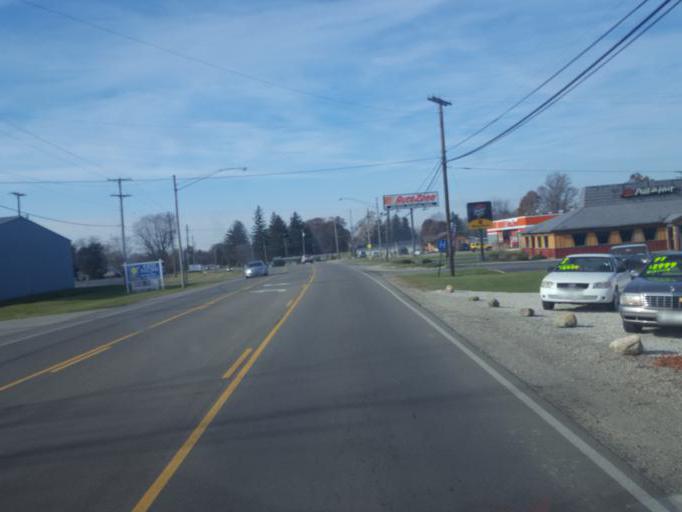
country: US
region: Ohio
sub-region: Crawford County
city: Bucyrus
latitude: 40.8125
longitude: -82.9514
